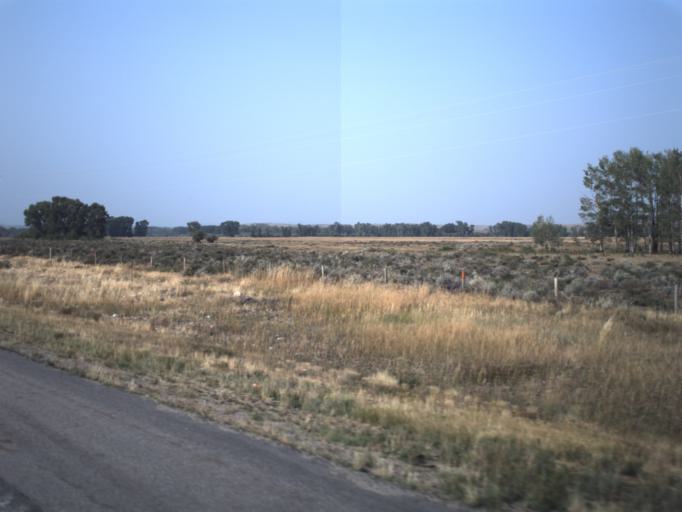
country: US
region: Wyoming
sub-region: Uinta County
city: Evanston
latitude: 40.9976
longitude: -110.8650
